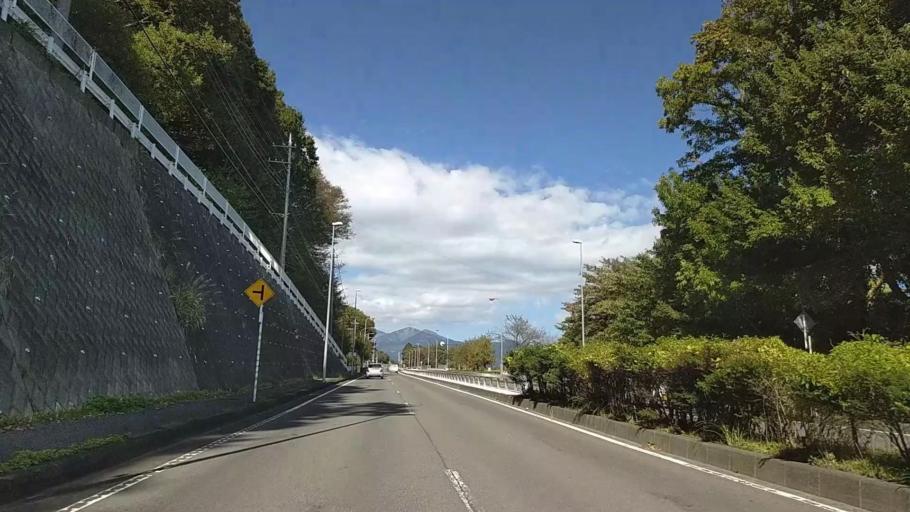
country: JP
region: Kanagawa
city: Ninomiya
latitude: 35.3299
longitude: 139.2323
